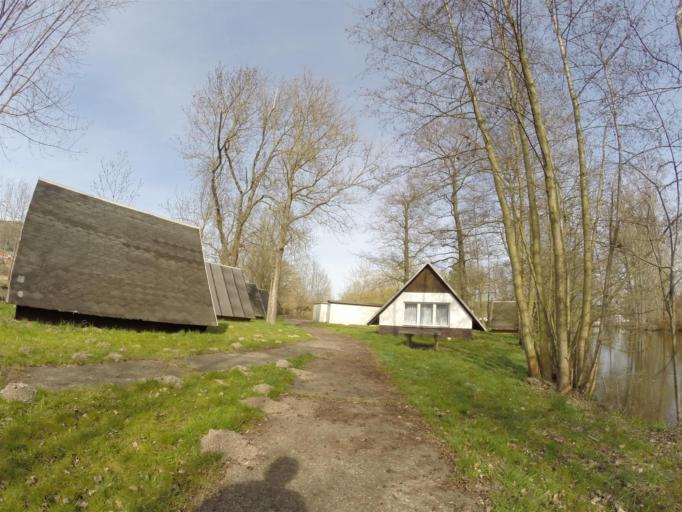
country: DE
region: Thuringia
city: Neuengonna
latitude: 50.9726
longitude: 11.6468
